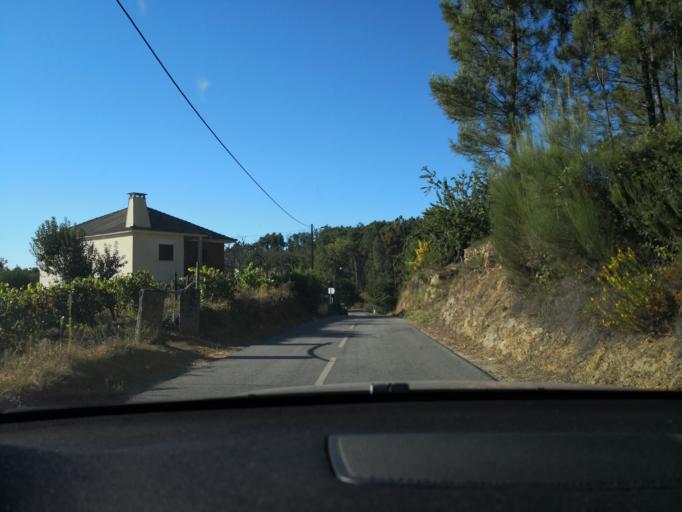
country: PT
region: Vila Real
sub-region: Sabrosa
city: Vilela
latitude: 41.2392
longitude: -7.6130
